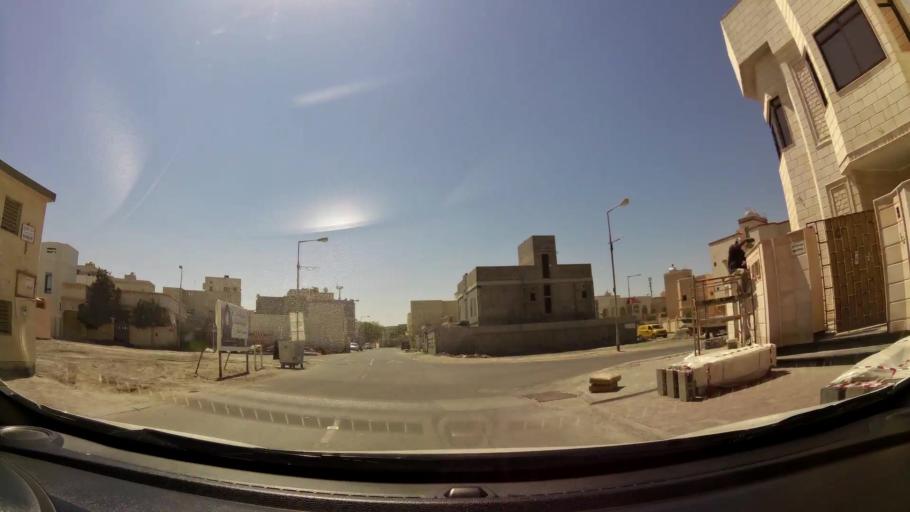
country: BH
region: Muharraq
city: Al Muharraq
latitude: 26.2814
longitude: 50.6390
